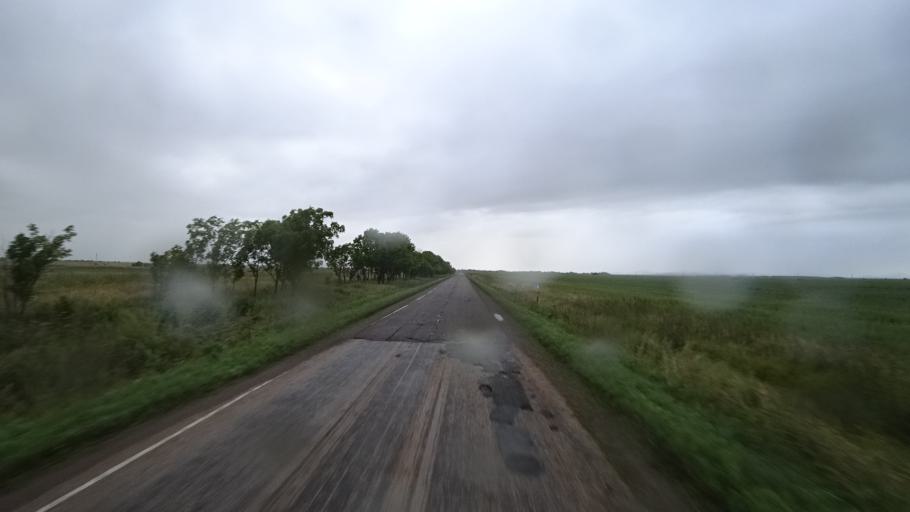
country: RU
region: Primorskiy
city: Chernigovka
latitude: 44.3823
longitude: 132.5296
